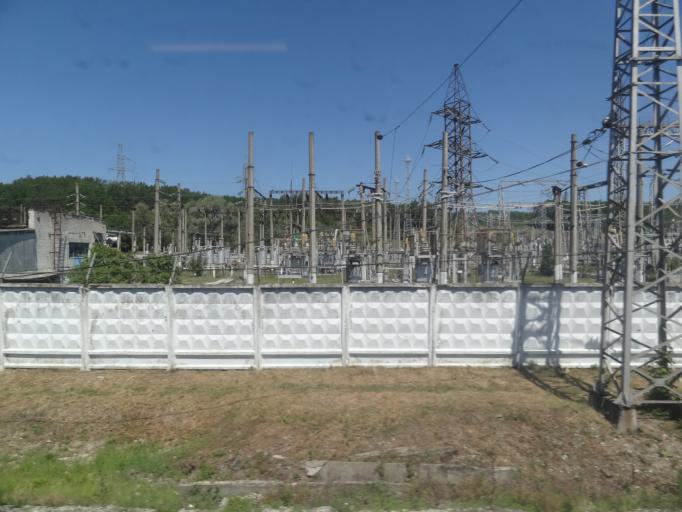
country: RU
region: Krasnodarskiy
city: Goryachiy Klyuch
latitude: 44.6419
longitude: 39.1153
